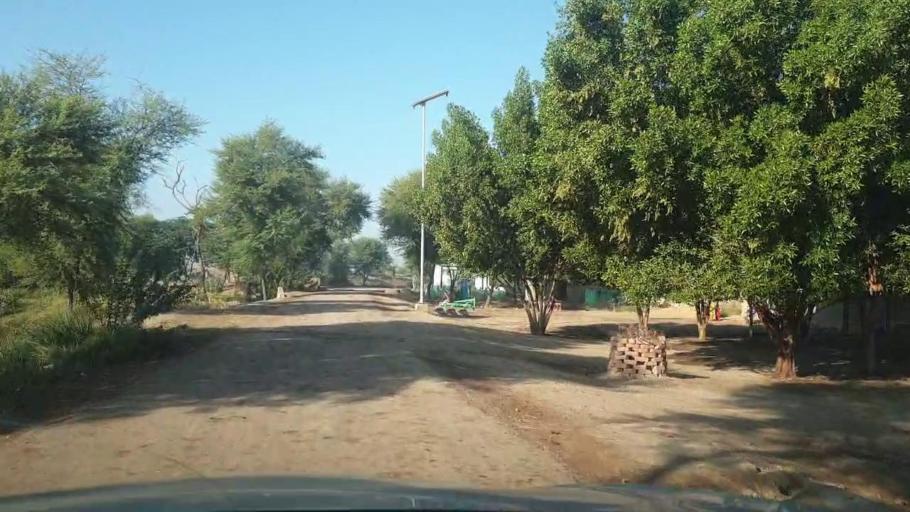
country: PK
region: Sindh
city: Bhan
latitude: 26.5546
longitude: 67.6860
